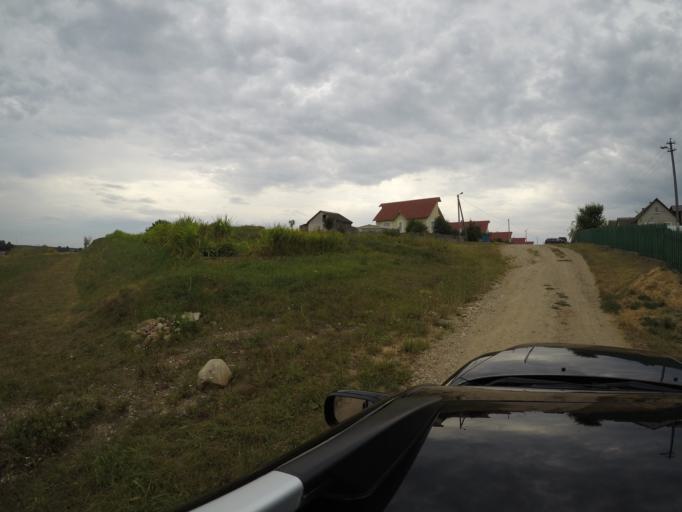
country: BY
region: Grodnenskaya
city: Hal'shany
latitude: 54.2598
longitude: 26.0089
